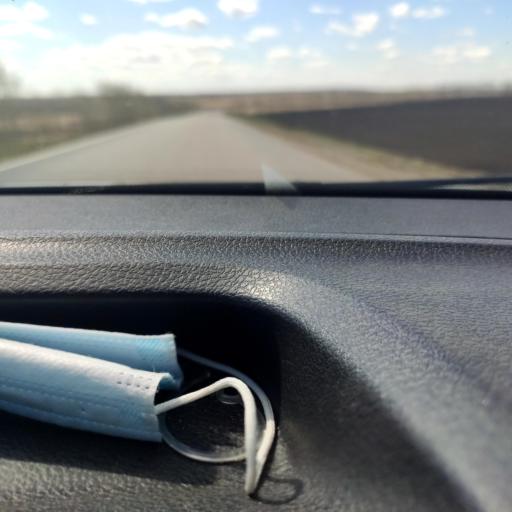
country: RU
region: Bashkortostan
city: Alekseyevka
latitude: 54.7766
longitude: 55.1792
